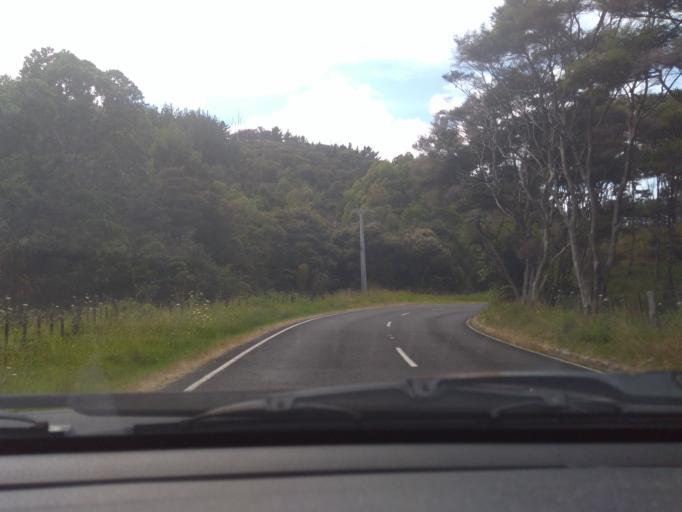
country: NZ
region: Northland
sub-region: Far North District
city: Taipa
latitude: -34.9872
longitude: 173.7057
